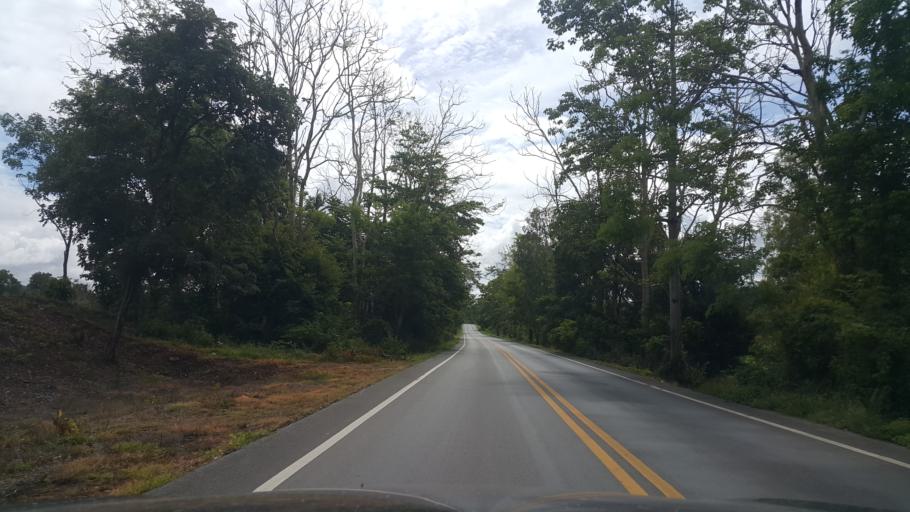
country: TH
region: Uttaradit
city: Thong Saen Khan
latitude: 17.3737
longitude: 100.2616
